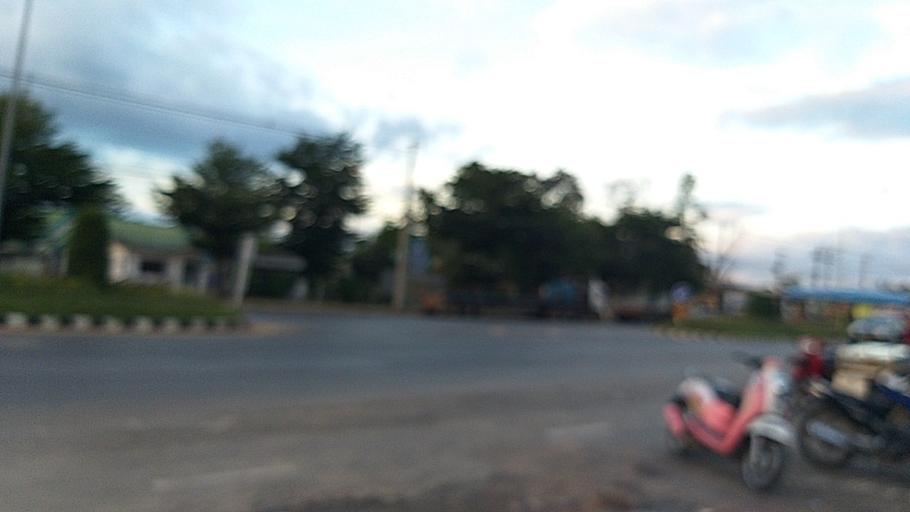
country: TH
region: Surin
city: Kap Choeng
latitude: 14.4529
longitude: 103.6910
